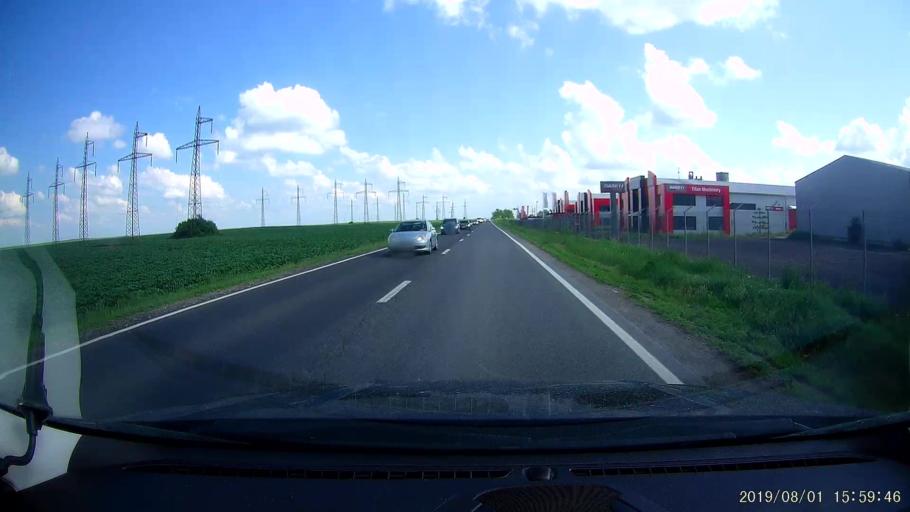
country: RO
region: Ialomita
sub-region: Comuna Slobozia
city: Slobozia
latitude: 44.5409
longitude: 27.3858
